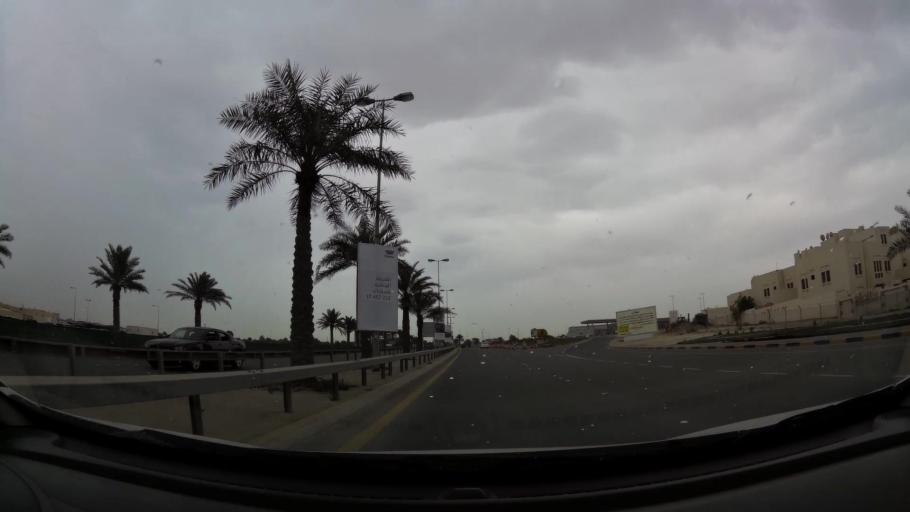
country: BH
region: Northern
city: Ar Rifa'
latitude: 26.1006
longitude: 50.5435
